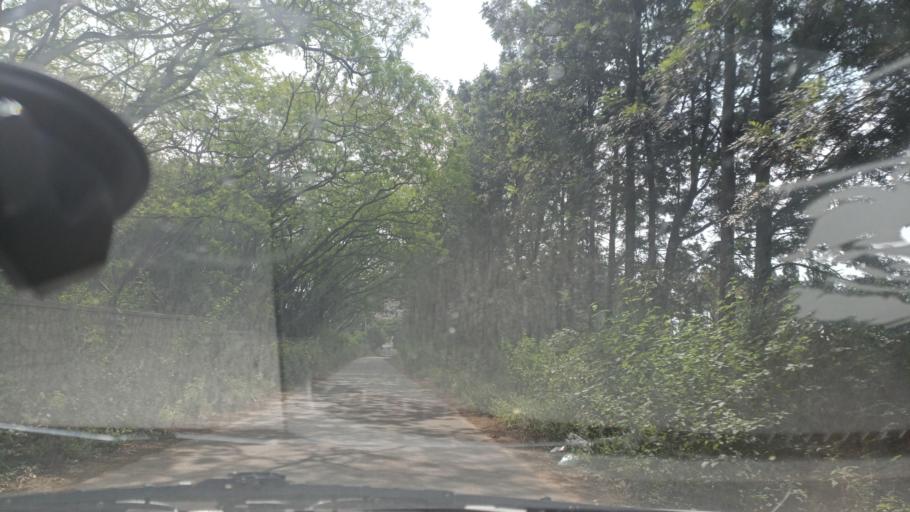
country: IN
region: Karnataka
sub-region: Bangalore Urban
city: Yelahanka
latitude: 13.1568
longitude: 77.6410
